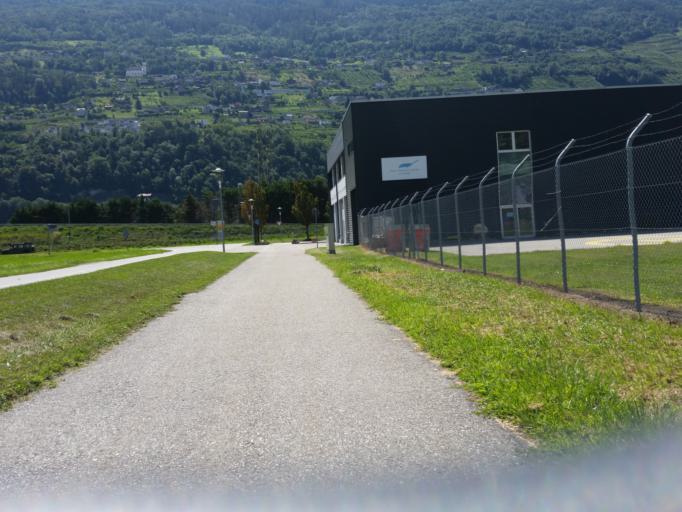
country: CH
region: Valais
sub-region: Sion District
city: Sitten
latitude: 46.2223
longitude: 7.3469
